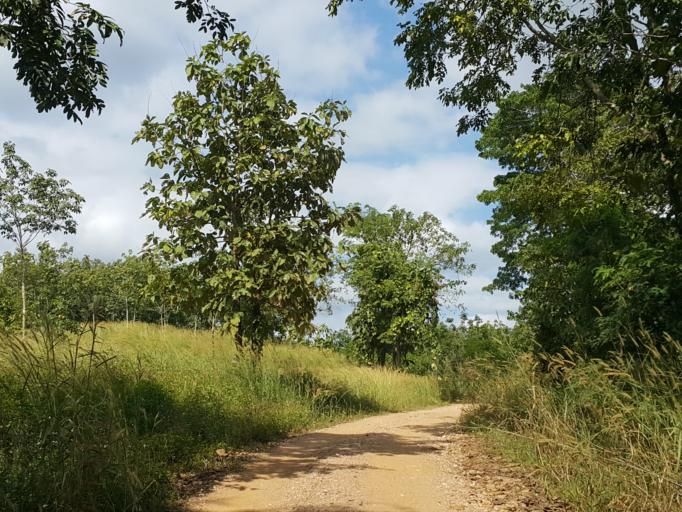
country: TH
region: Lampang
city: Hang Chat
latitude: 18.4821
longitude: 99.4157
